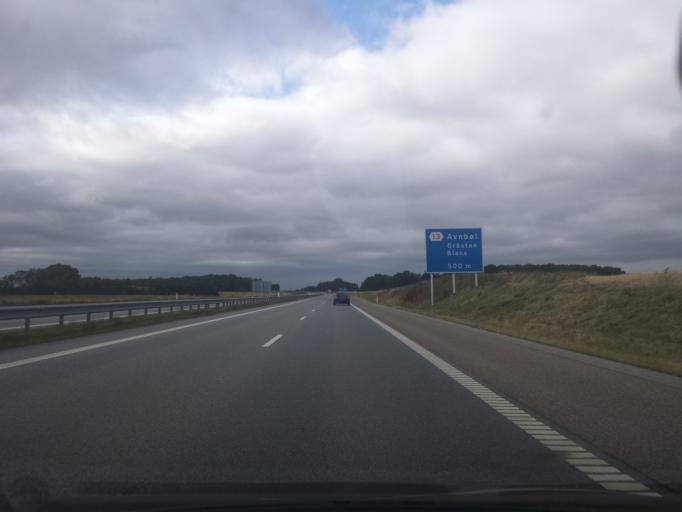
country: DK
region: South Denmark
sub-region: Sonderborg Kommune
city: Grasten
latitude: 54.9464
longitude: 9.6501
